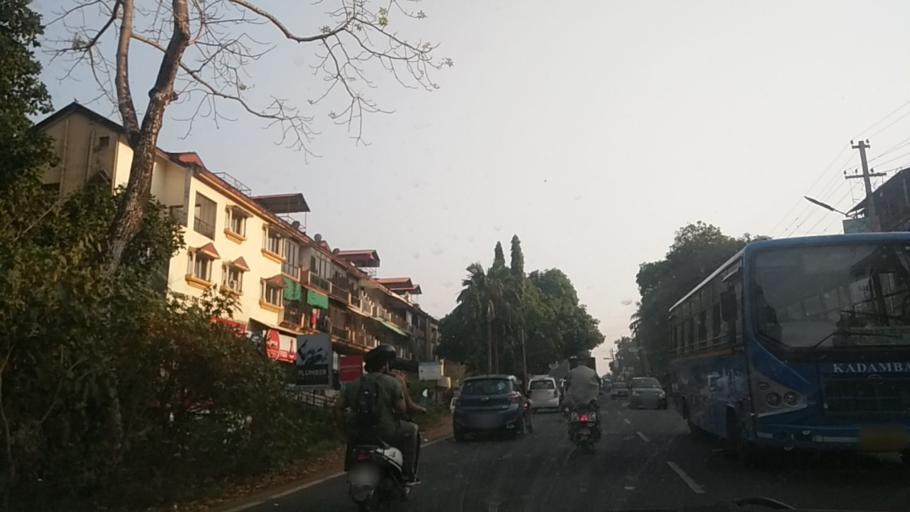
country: IN
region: Goa
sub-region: North Goa
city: Serula
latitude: 15.5435
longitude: 73.8209
